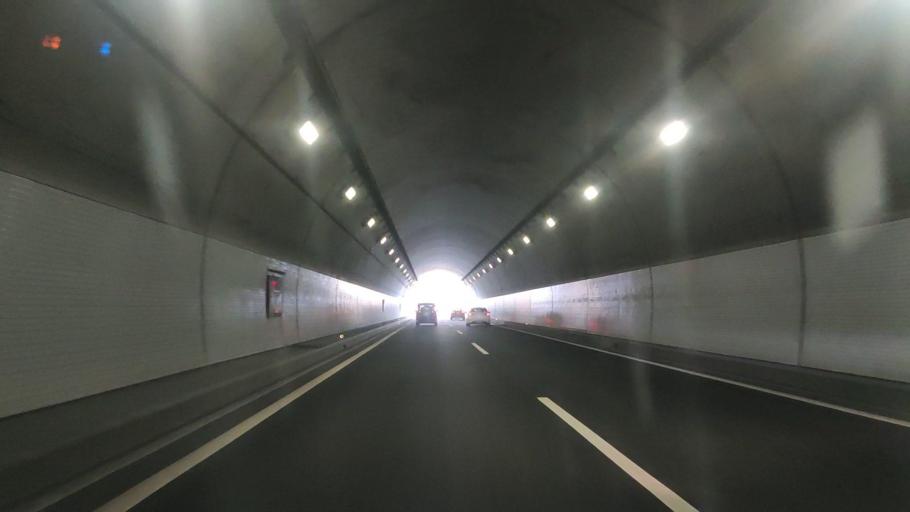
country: JP
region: Fukuoka
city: Kitakyushu
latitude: 33.8122
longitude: 130.9087
